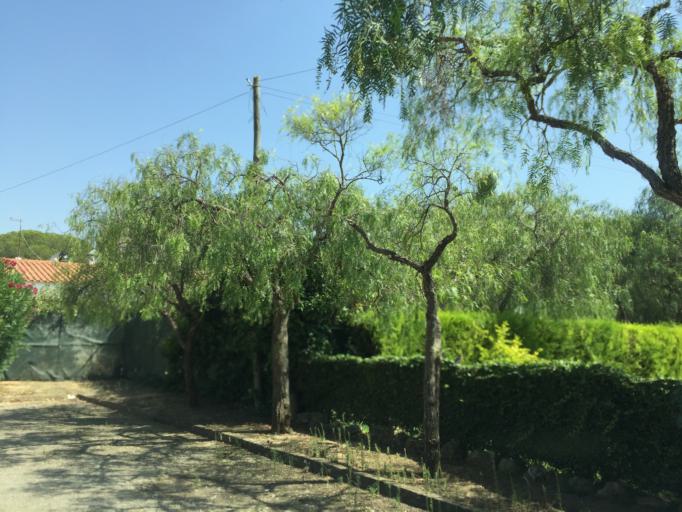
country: PT
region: Faro
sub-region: Albufeira
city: Ferreiras
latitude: 37.1039
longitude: -8.2024
